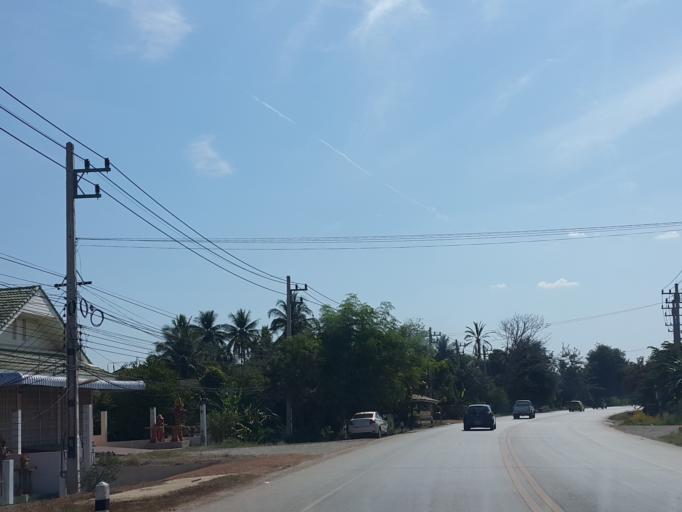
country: TH
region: Sukhothai
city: Sawankhalok
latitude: 17.2873
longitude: 99.8435
